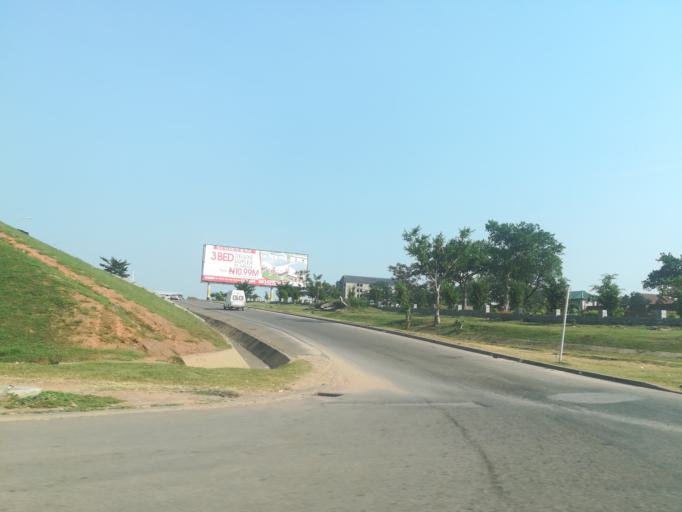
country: NG
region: Abuja Federal Capital Territory
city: Abuja
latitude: 9.0786
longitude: 7.4280
